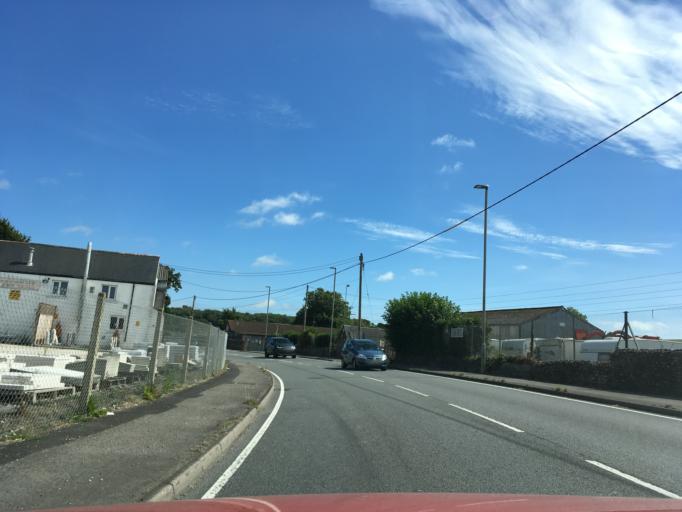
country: GB
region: England
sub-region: Dorset
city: Dorchester
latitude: 50.7457
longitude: -2.5124
